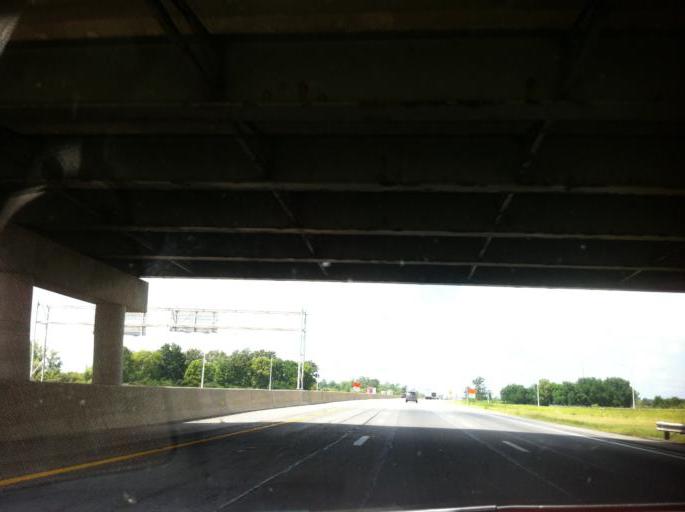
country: US
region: Ohio
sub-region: Huron County
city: Bellevue
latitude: 41.3410
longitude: -82.7657
